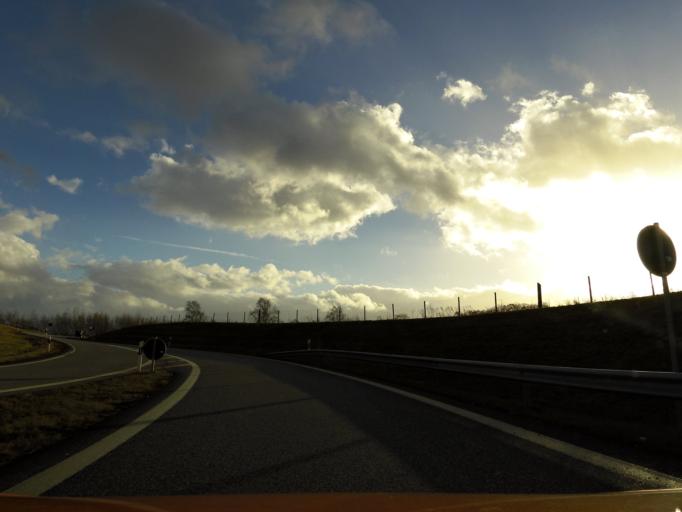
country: DE
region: Lower Saxony
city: Langwedel
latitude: 53.0007
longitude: 9.1746
